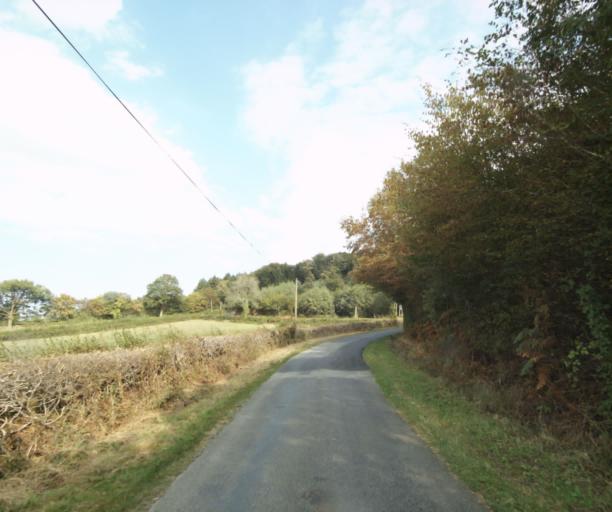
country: FR
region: Bourgogne
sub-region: Departement de Saone-et-Loire
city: Palinges
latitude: 46.5103
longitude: 4.2738
